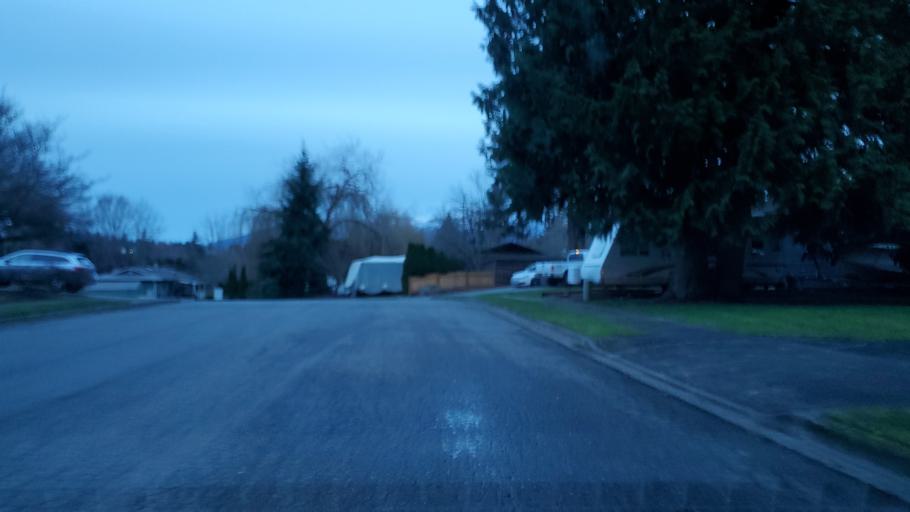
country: US
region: Washington
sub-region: Skagit County
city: Mount Vernon
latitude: 48.4406
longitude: -122.3224
